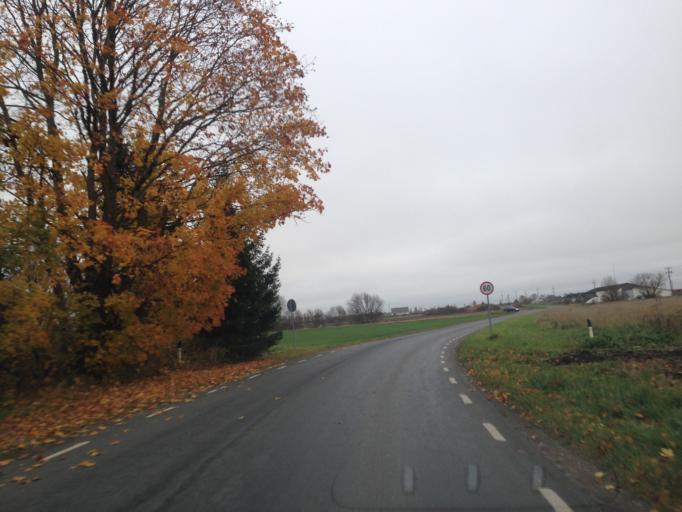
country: EE
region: Harju
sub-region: Saue linn
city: Saue
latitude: 59.3540
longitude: 24.5580
